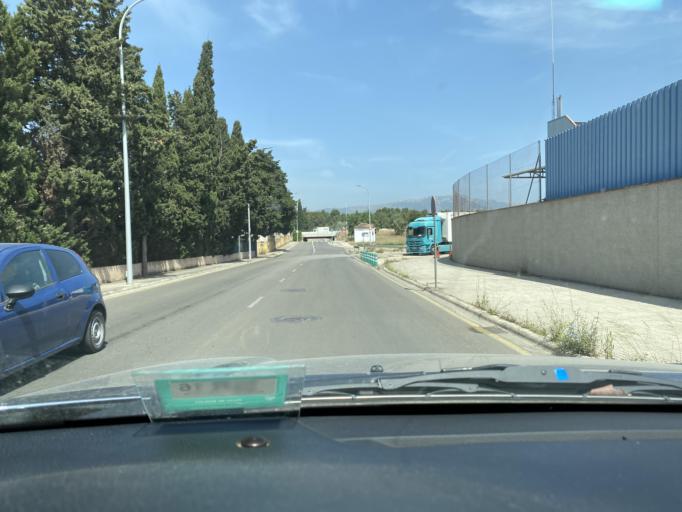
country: ES
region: Balearic Islands
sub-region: Illes Balears
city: Marratxi
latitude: 39.6216
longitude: 2.7125
